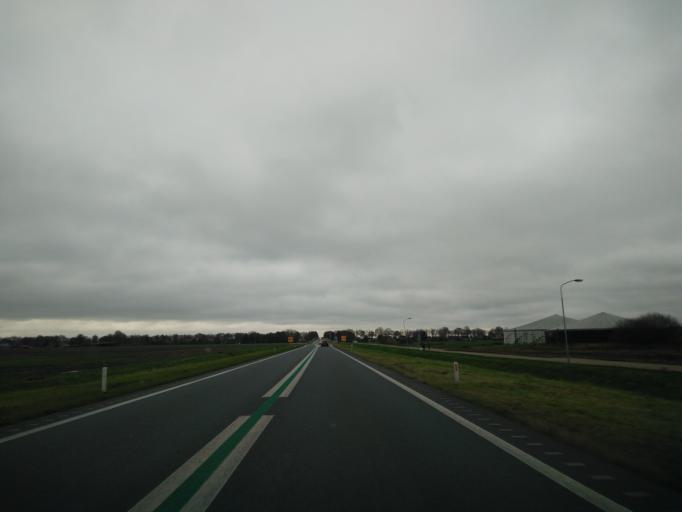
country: NL
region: Drenthe
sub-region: Gemeente Emmen
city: Emmer-Compascuum
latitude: 52.8815
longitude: 7.0395
